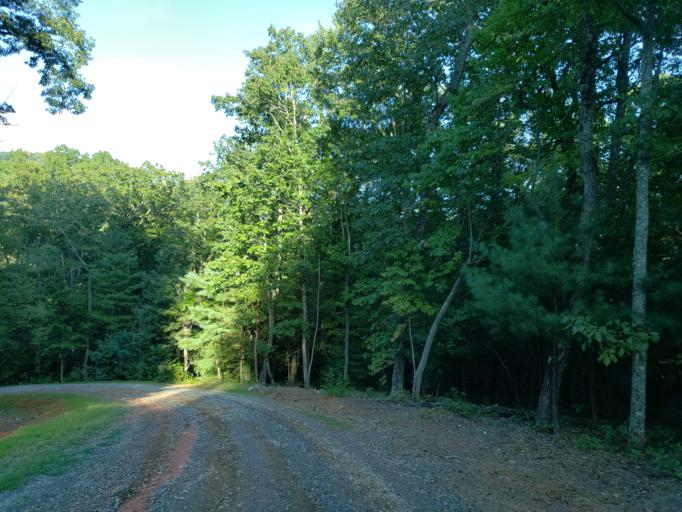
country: US
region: Georgia
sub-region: Fannin County
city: Blue Ridge
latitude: 34.6887
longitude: -84.2745
